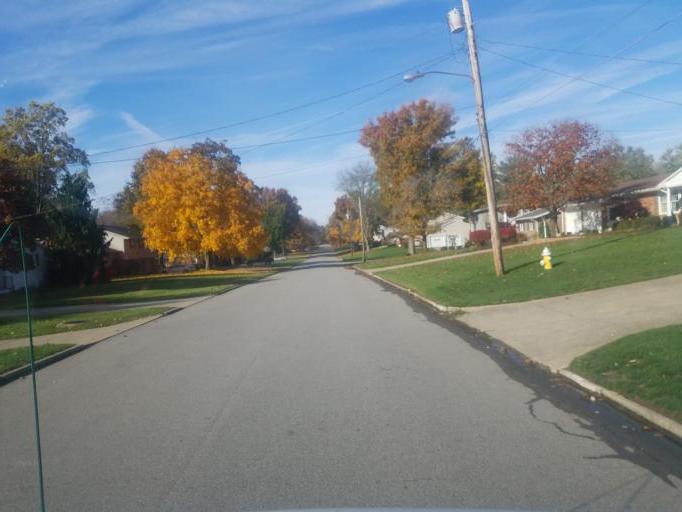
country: US
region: Ohio
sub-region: Richland County
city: Mansfield
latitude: 40.7262
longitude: -82.5170
